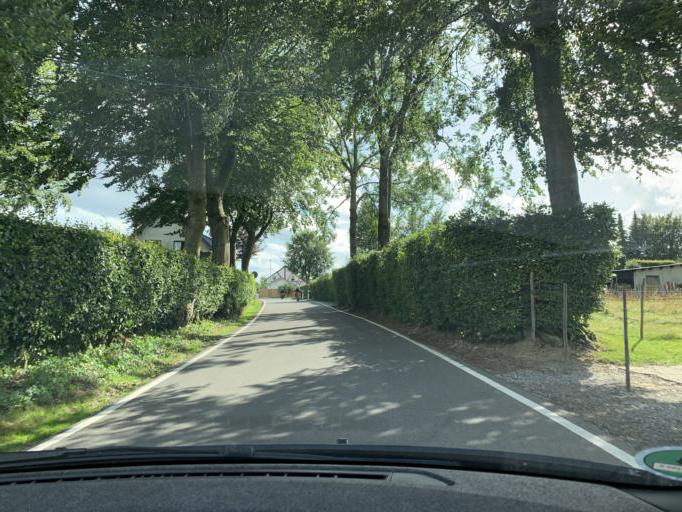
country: DE
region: North Rhine-Westphalia
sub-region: Regierungsbezirk Koln
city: Simmerath
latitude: 50.5962
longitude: 6.2587
